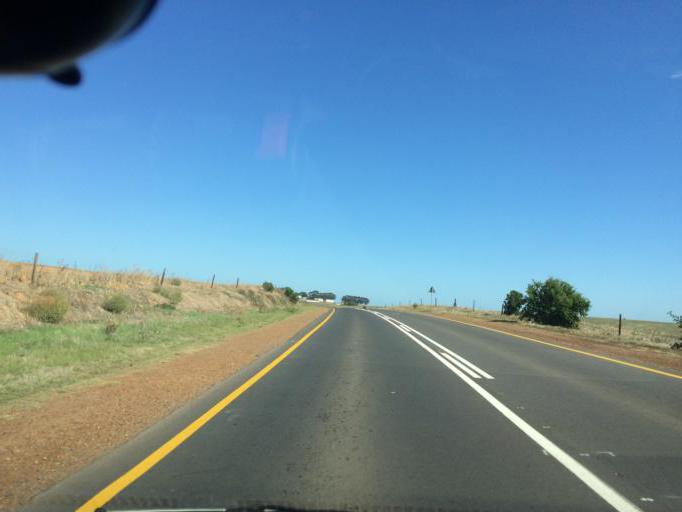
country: ZA
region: Western Cape
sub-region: City of Cape Town
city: Atlantis
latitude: -33.6663
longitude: 18.5760
